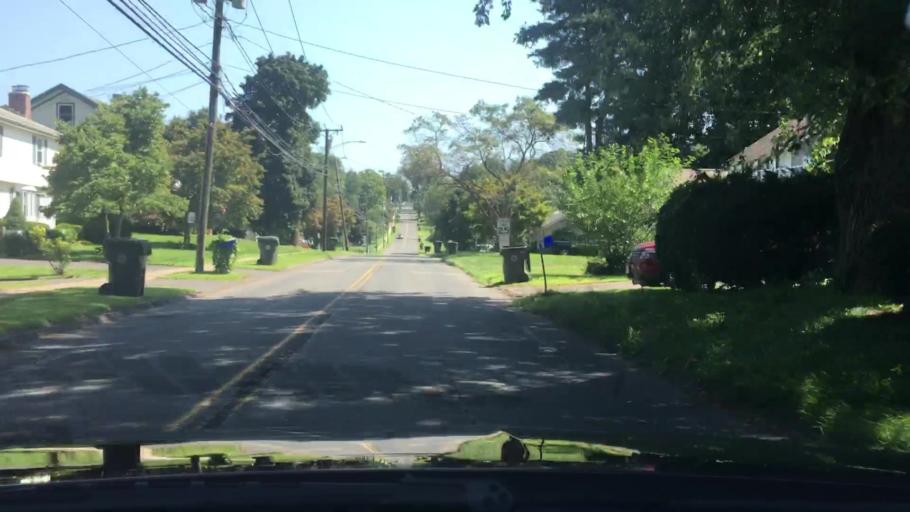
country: US
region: Connecticut
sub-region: Hartford County
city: Kensington
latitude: 41.6169
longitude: -72.7541
